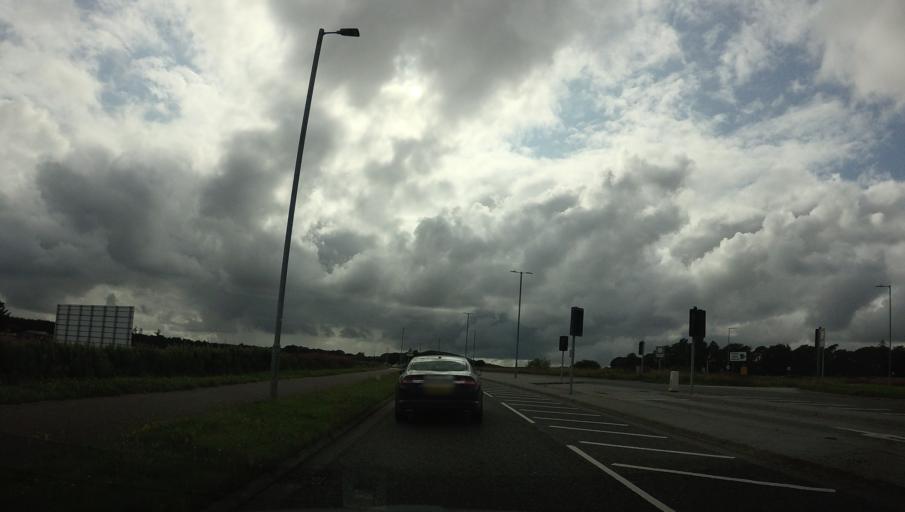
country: GB
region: Scotland
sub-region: Aberdeen City
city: Cults
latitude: 57.1498
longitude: -2.1954
